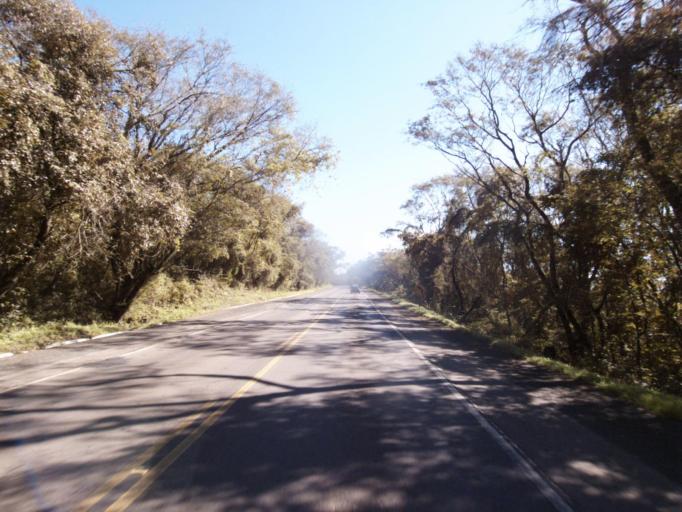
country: BR
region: Rio Grande do Sul
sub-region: Frederico Westphalen
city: Frederico Westphalen
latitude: -26.7989
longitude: -53.3387
